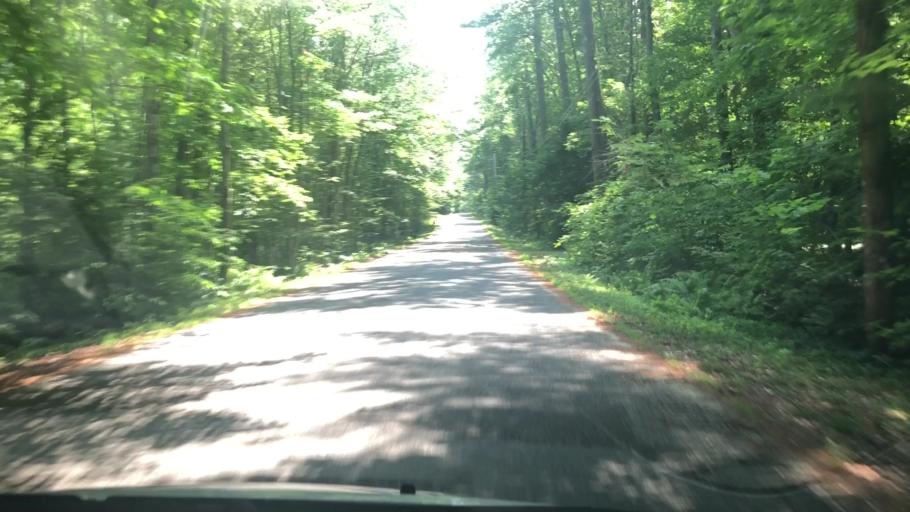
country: US
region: New Hampshire
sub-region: Hillsborough County
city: Milford
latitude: 42.8750
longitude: -71.6326
